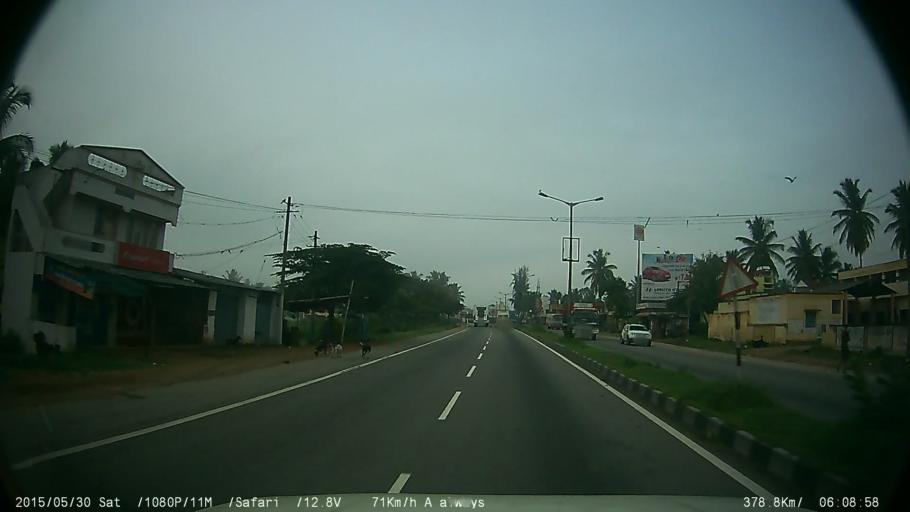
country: IN
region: Karnataka
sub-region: Mandya
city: Shrirangapattana
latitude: 12.3650
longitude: 76.6616
